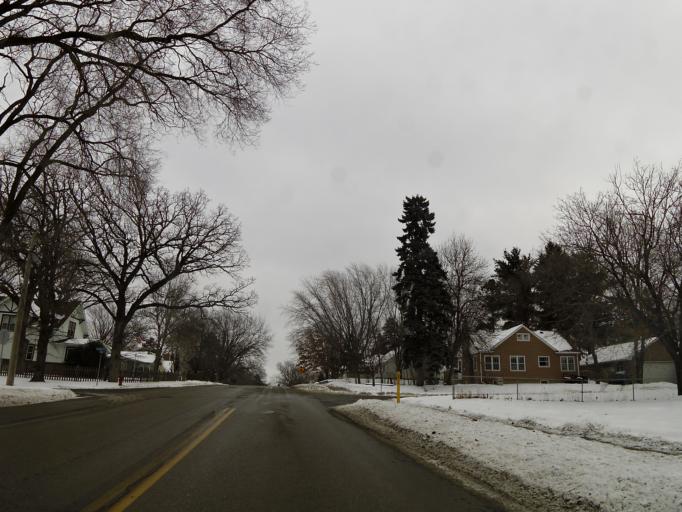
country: US
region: Minnesota
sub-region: Ramsey County
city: North Saint Paul
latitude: 45.0064
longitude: -93.0004
